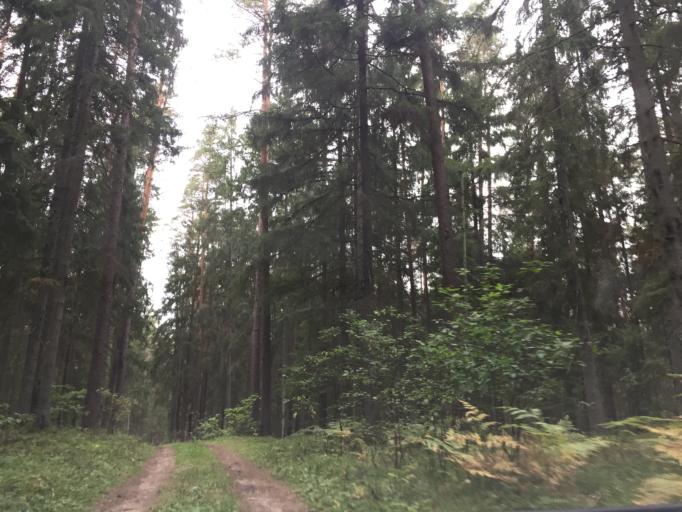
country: LV
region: Baldone
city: Baldone
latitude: 56.7727
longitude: 24.4518
